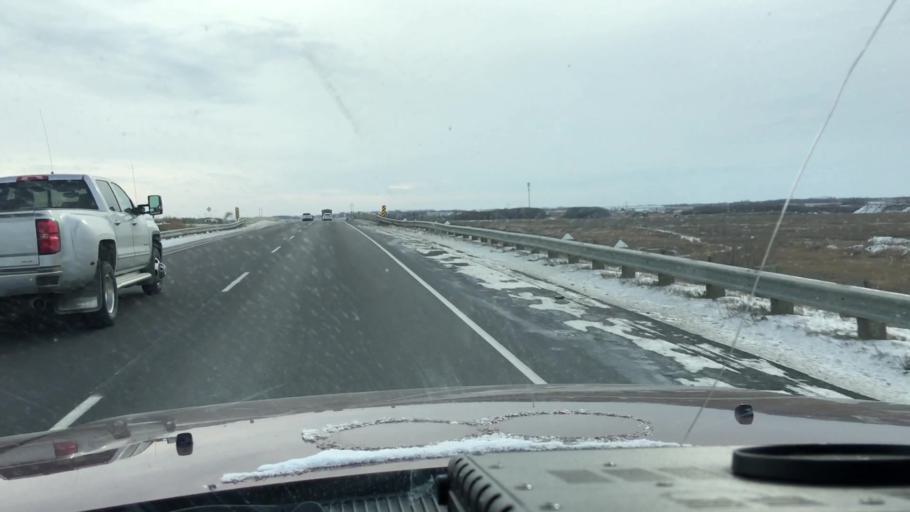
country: CA
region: Saskatchewan
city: Saskatoon
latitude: 52.0705
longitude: -106.6036
